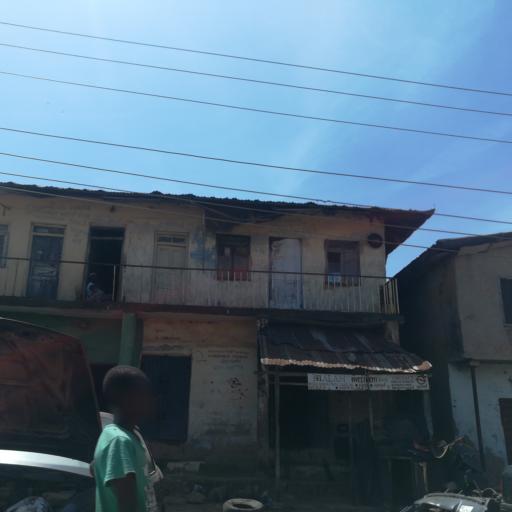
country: NG
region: Plateau
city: Bukuru
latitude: 9.7978
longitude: 8.8641
